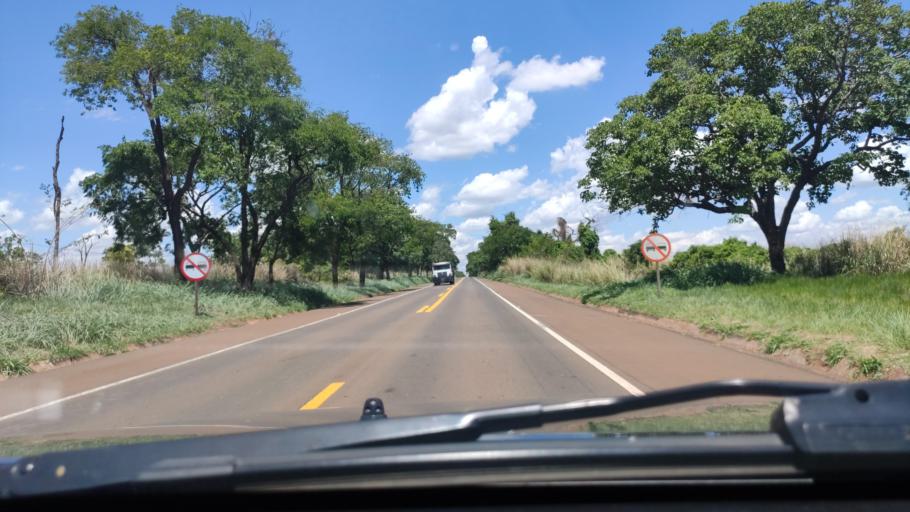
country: BR
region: Sao Paulo
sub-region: Boa Esperanca Do Sul
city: Boa Esperanca do Sul
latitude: -22.0693
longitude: -48.3929
